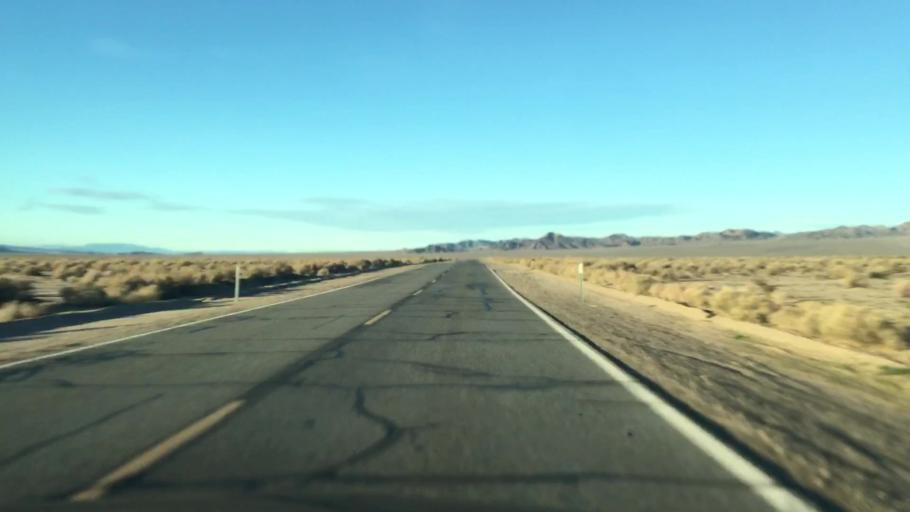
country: US
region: California
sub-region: San Bernardino County
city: Fort Irwin
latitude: 35.3044
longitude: -116.0835
